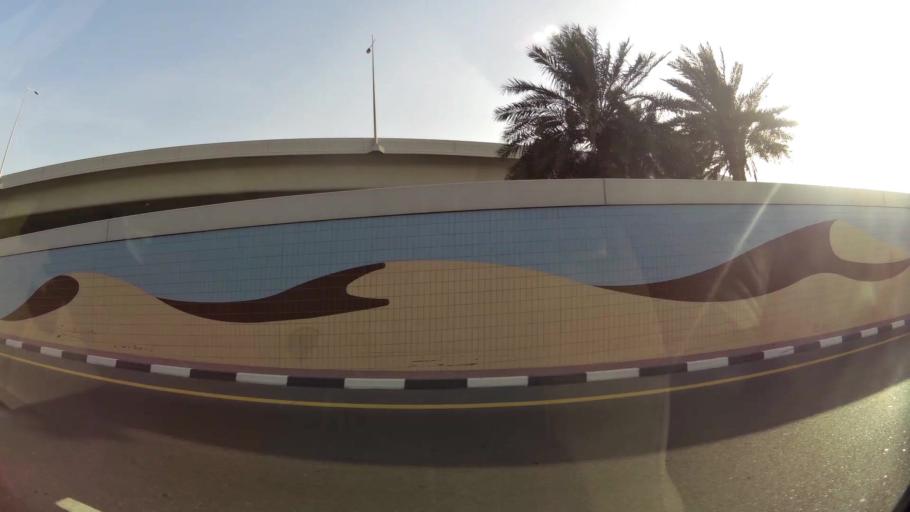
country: AE
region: Ash Shariqah
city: Sharjah
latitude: 25.2287
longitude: 55.3545
